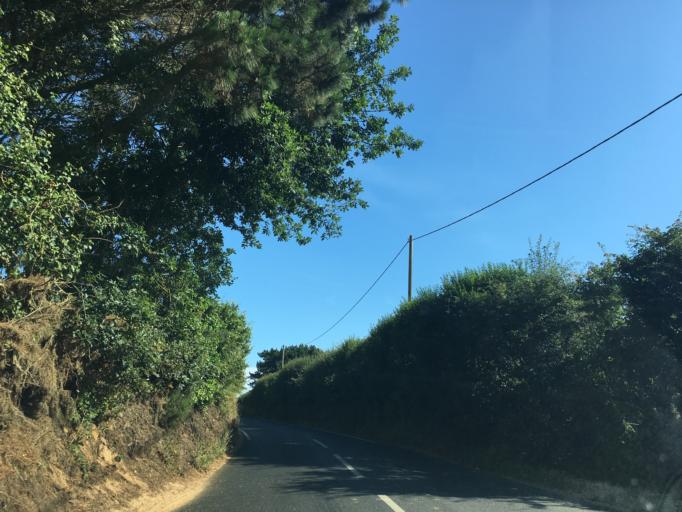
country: GB
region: England
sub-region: Isle of Wight
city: Chale
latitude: 50.6192
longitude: -1.3210
